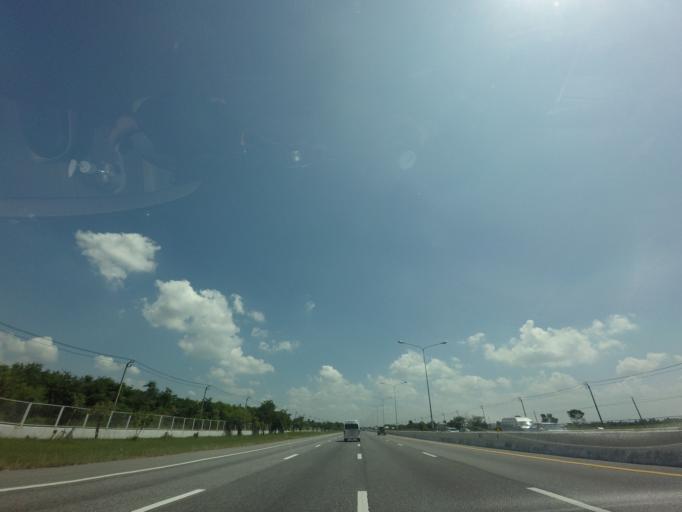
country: TH
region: Chachoengsao
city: Bang Pakong
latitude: 13.6156
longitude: 100.9287
